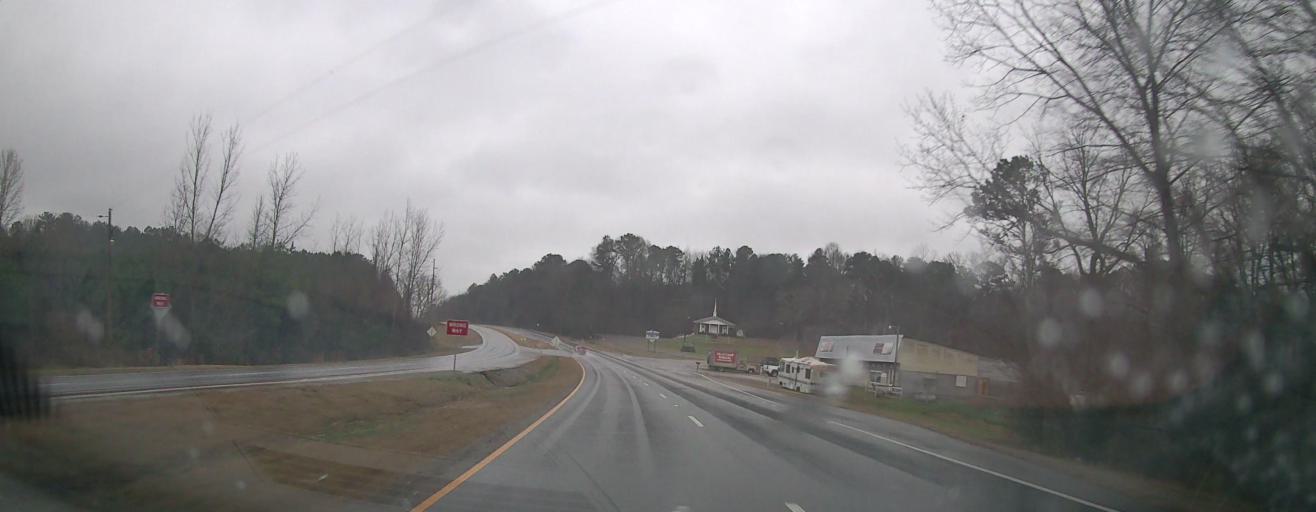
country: US
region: Alabama
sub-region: Morgan County
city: Flint City
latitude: 34.5095
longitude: -86.9696
